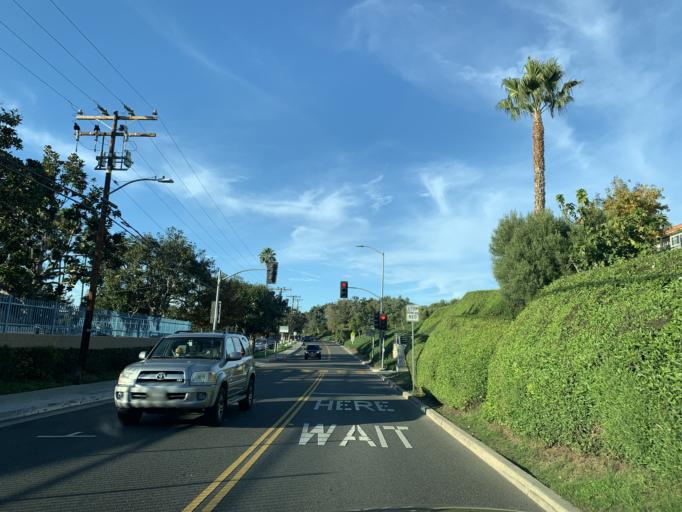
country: US
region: California
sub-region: Los Angeles County
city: Hermosa Beach
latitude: 33.8663
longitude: -118.3959
